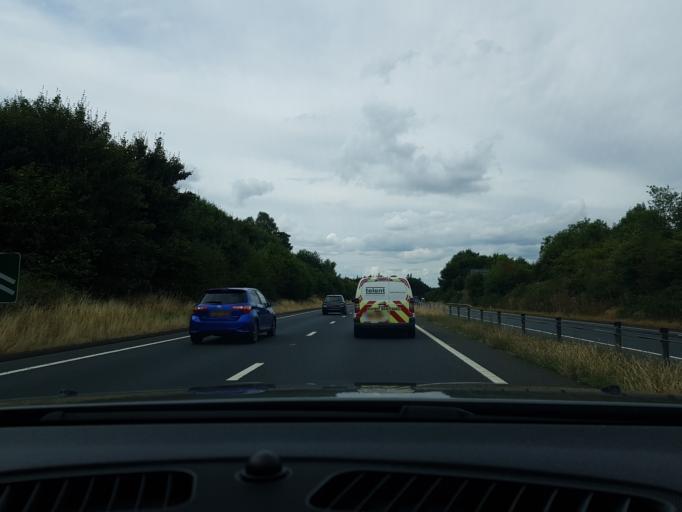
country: GB
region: England
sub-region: Hampshire
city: Highclere
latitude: 51.3612
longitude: -1.3537
